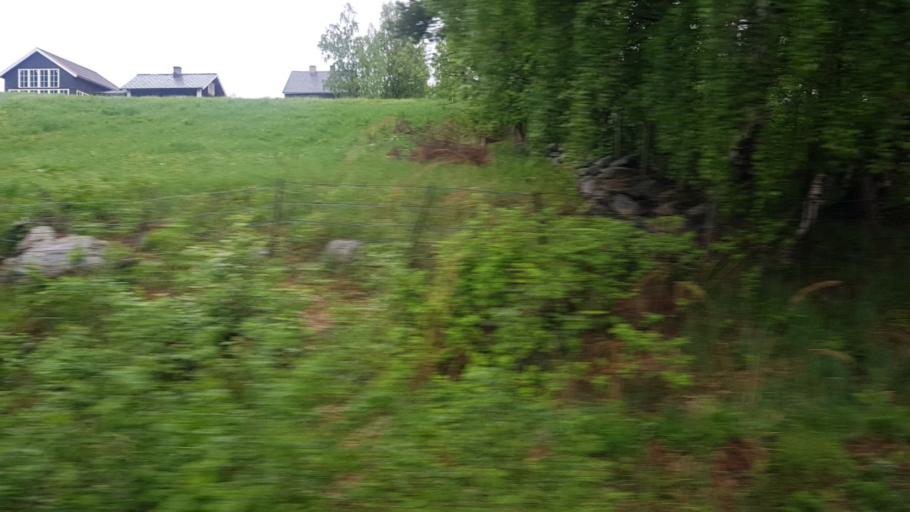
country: NO
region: Oppland
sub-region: Sor-Fron
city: Hundorp
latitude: 61.5586
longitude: 9.9374
